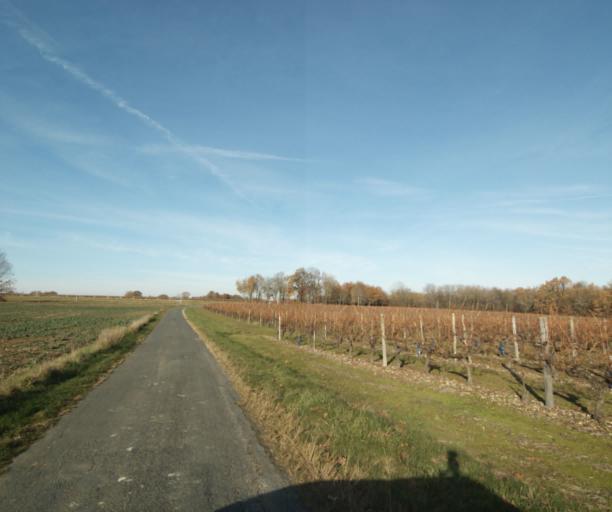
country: FR
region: Poitou-Charentes
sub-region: Departement de la Charente-Maritime
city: Cherac
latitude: 45.7492
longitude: -0.4818
